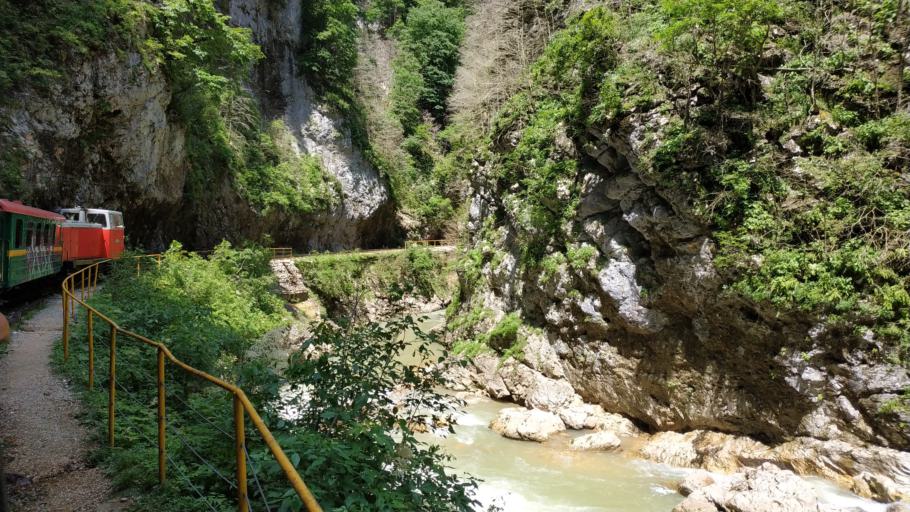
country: RU
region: Krasnodarskiy
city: Neftegorsk
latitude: 44.2185
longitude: 39.9083
